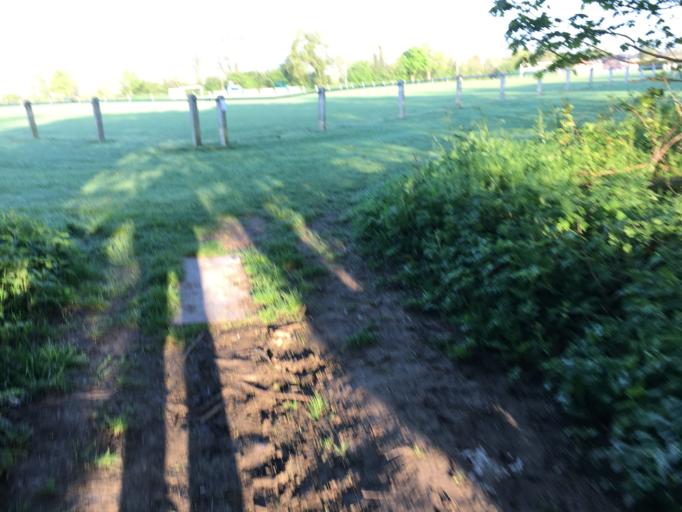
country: GB
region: England
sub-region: Leicestershire
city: Houghton on the Hill
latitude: 52.6236
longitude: -0.9922
